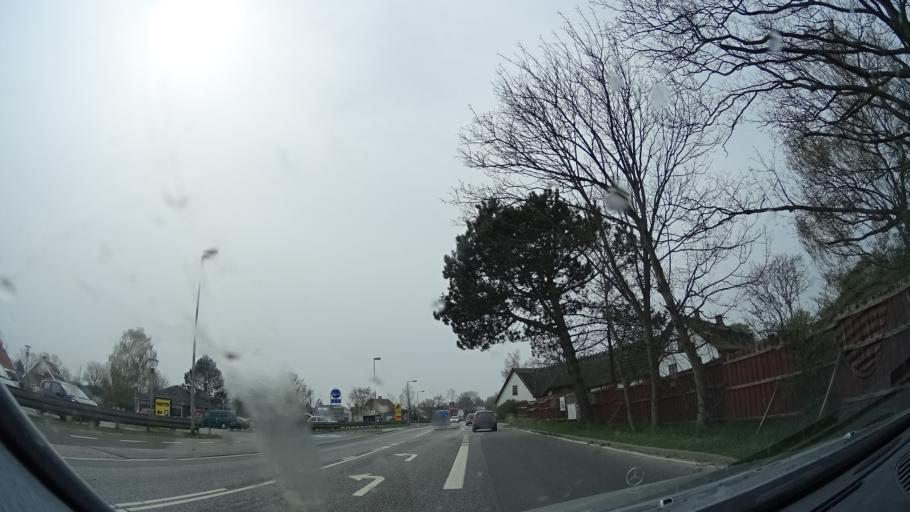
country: DK
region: Zealand
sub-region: Lejre Kommune
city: Ejby
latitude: 55.6897
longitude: 11.8580
